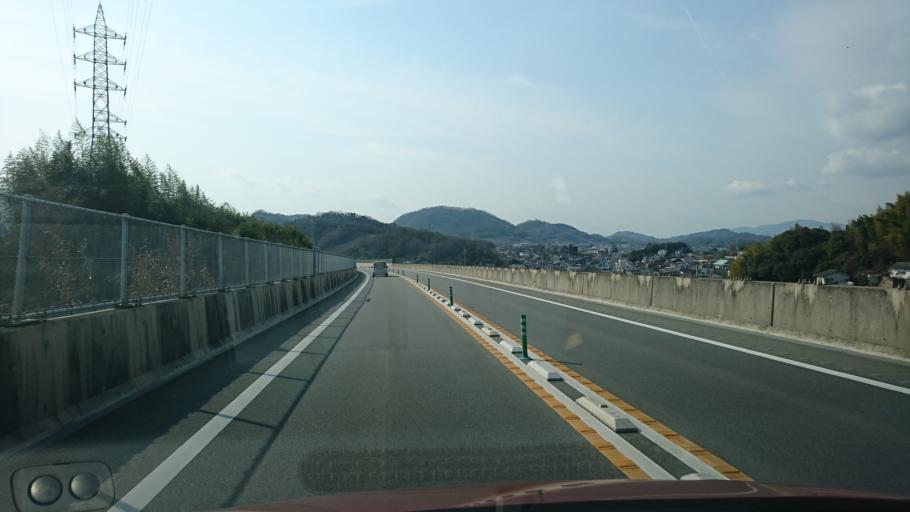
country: JP
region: Hiroshima
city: Onomichi
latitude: 34.4017
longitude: 133.2105
